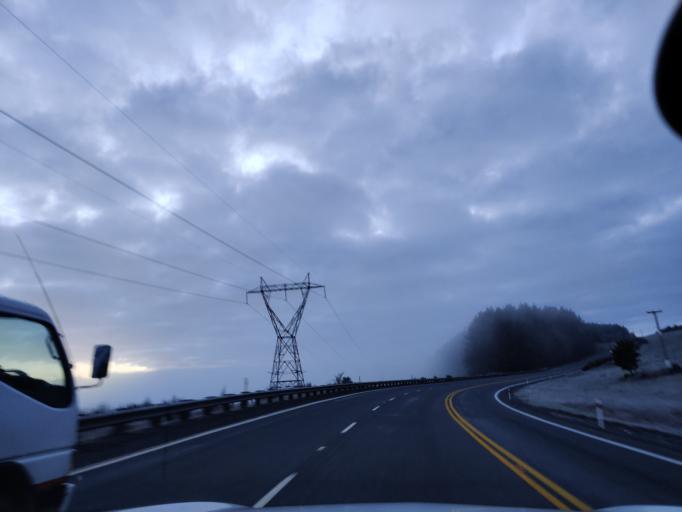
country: NZ
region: Waikato
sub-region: South Waikato District
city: Tokoroa
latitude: -38.3961
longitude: 176.0364
